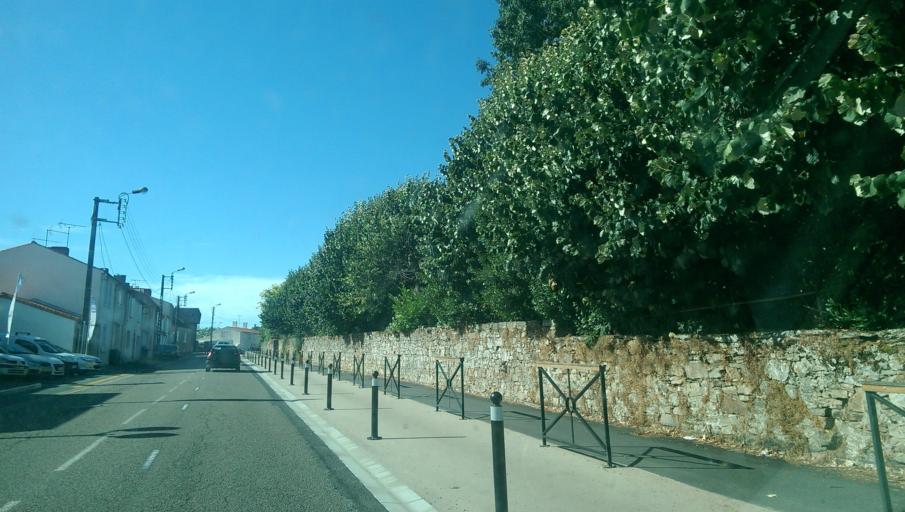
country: FR
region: Pays de la Loire
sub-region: Departement de la Vendee
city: Aizenay
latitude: 46.7411
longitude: -1.6098
